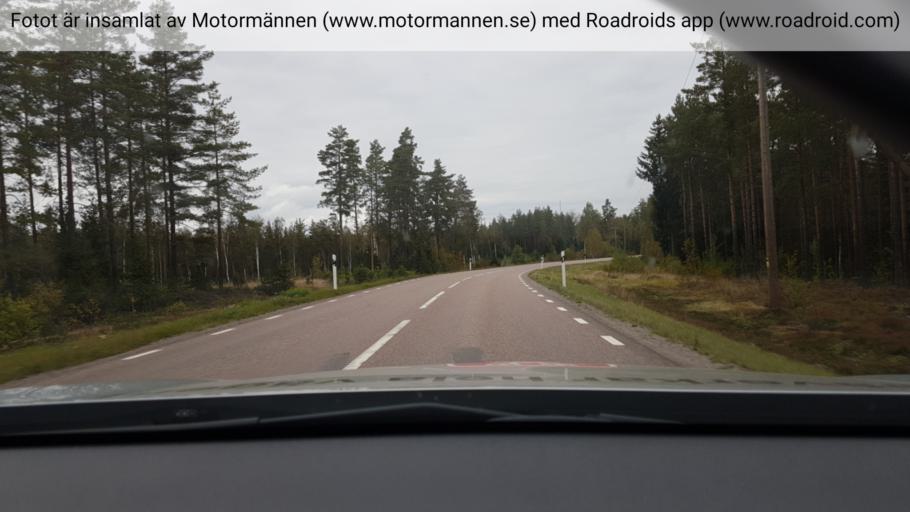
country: SE
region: Gaevleborg
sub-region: Gavle Kommun
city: Hedesunda
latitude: 60.5291
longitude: 16.9423
